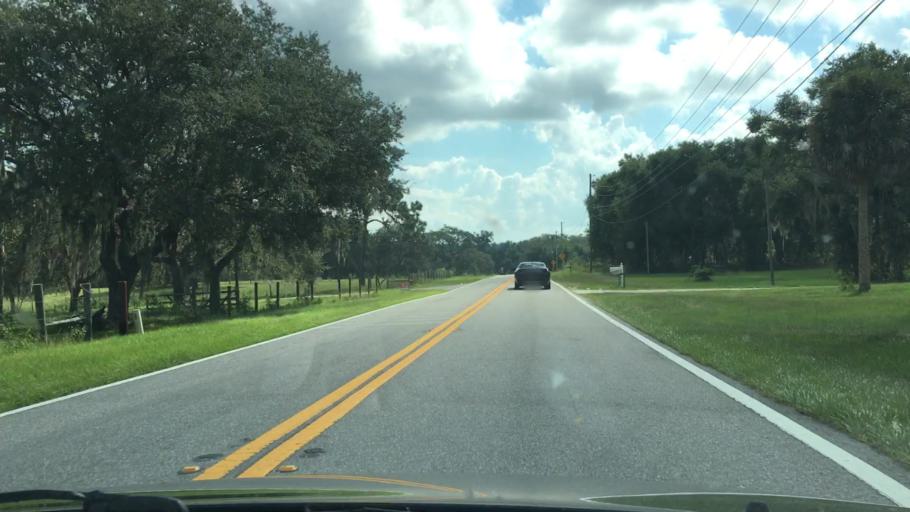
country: US
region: Florida
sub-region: Lake County
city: Astatula
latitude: 28.6668
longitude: -81.7349
